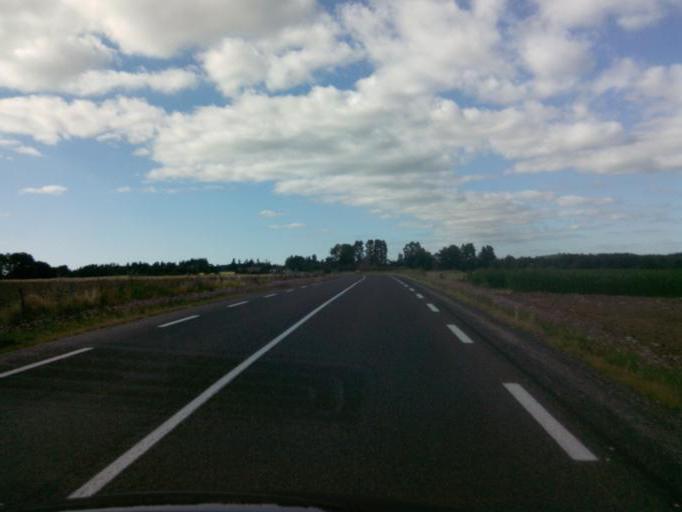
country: FR
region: Auvergne
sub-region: Departement de la Haute-Loire
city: Saint-Paulien
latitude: 45.1927
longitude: 3.8225
